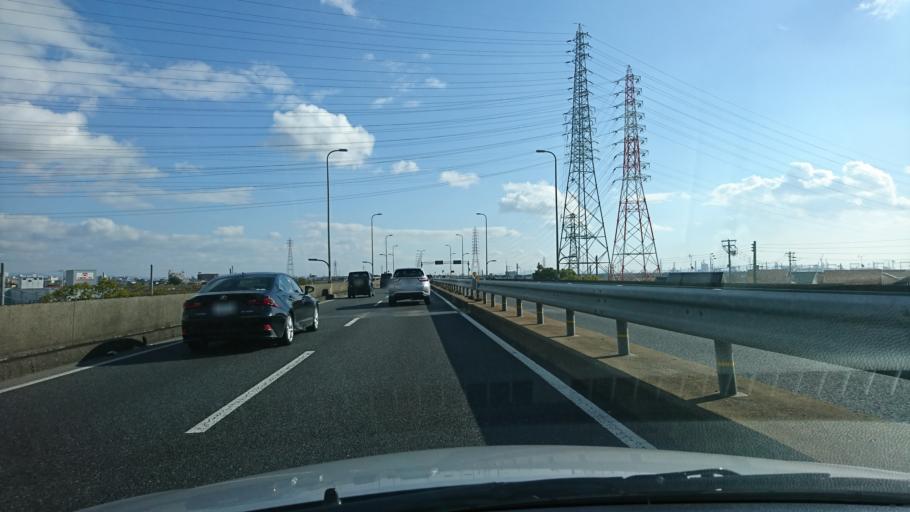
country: JP
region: Hyogo
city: Kakogawacho-honmachi
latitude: 34.7680
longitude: 134.8061
